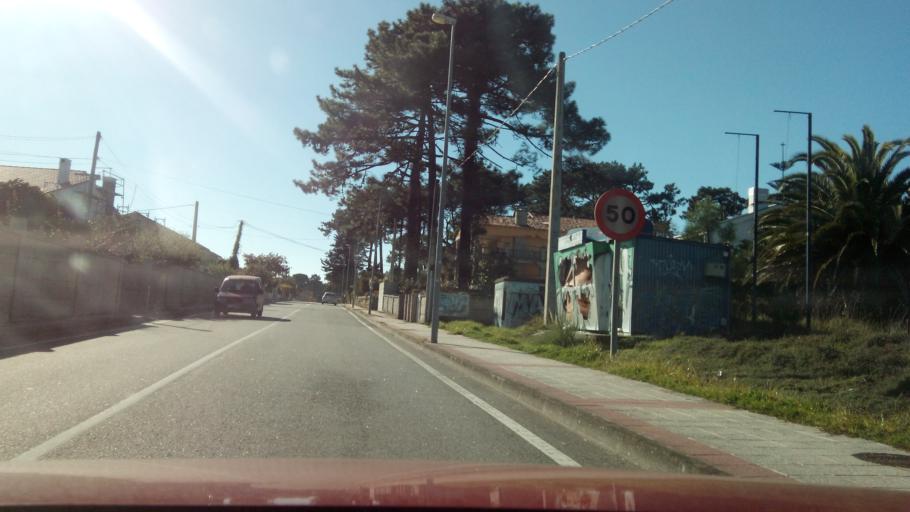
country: ES
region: Galicia
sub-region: Provincia de Pontevedra
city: O Grove
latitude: 42.4592
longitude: -8.9213
